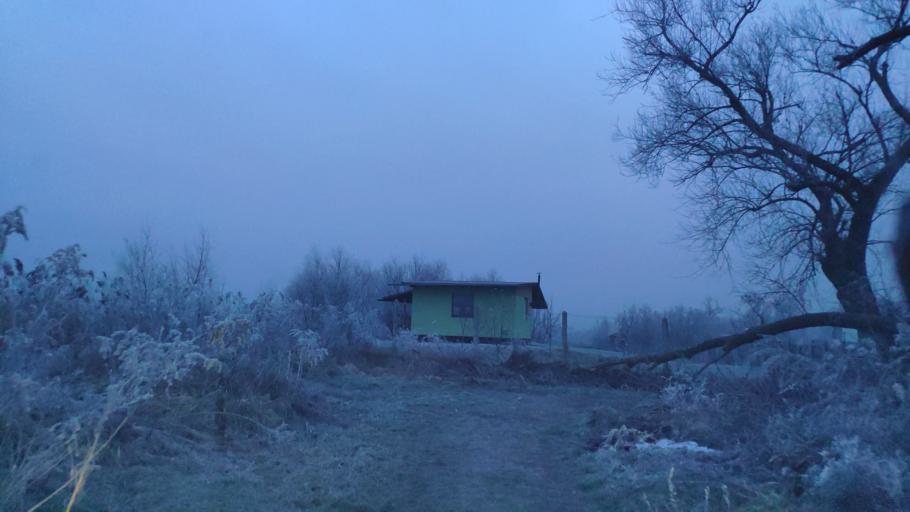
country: SK
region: Kosicky
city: Kosice
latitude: 48.6127
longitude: 21.3354
